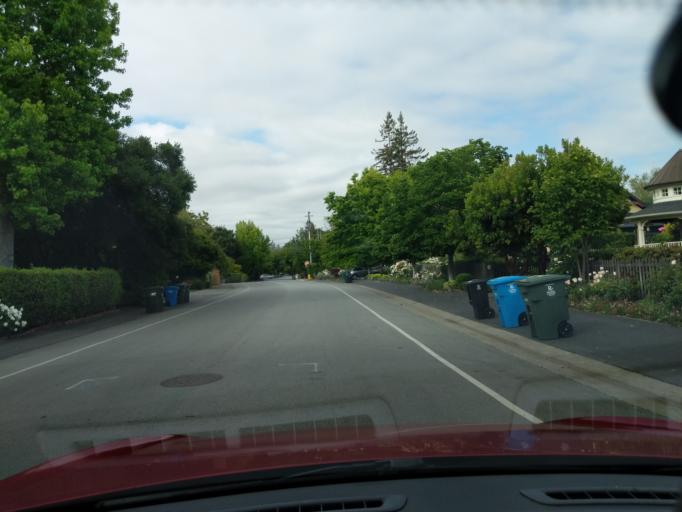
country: US
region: California
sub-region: San Mateo County
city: West Menlo Park
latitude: 37.4336
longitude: -122.1927
